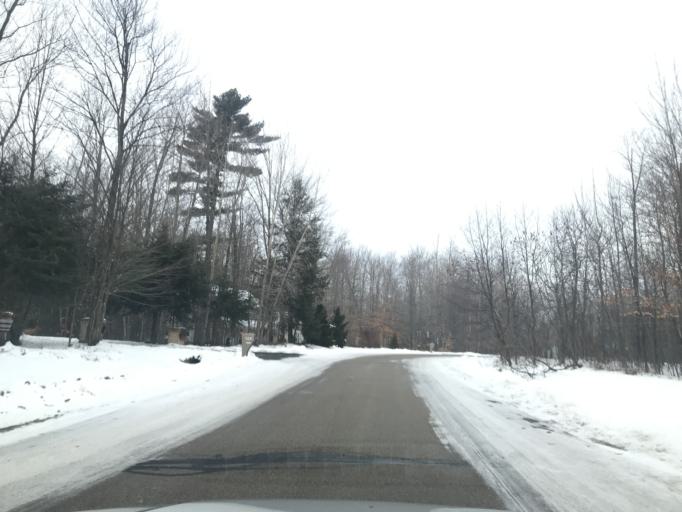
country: US
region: Wisconsin
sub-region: Brown County
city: Suamico
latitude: 44.6876
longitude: -88.0628
